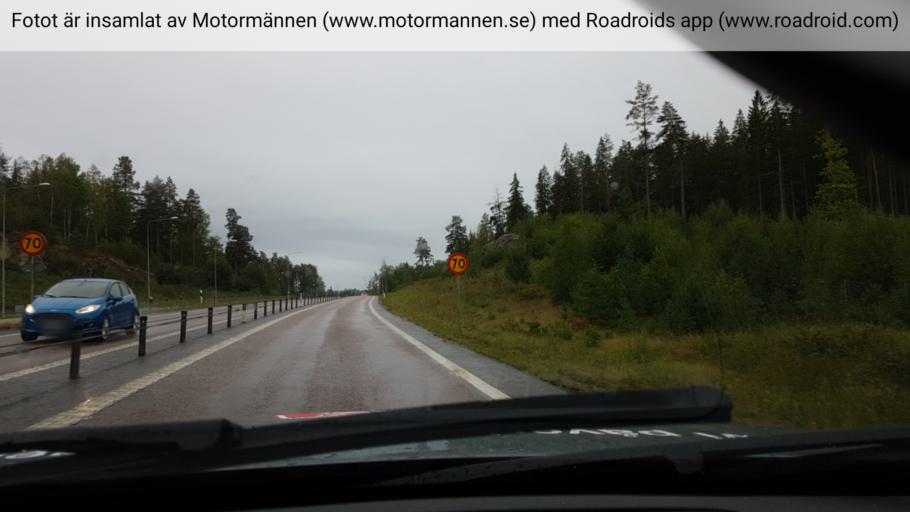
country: SE
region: Soedermanland
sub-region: Flens Kommun
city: Malmkoping
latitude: 59.1415
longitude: 16.7130
